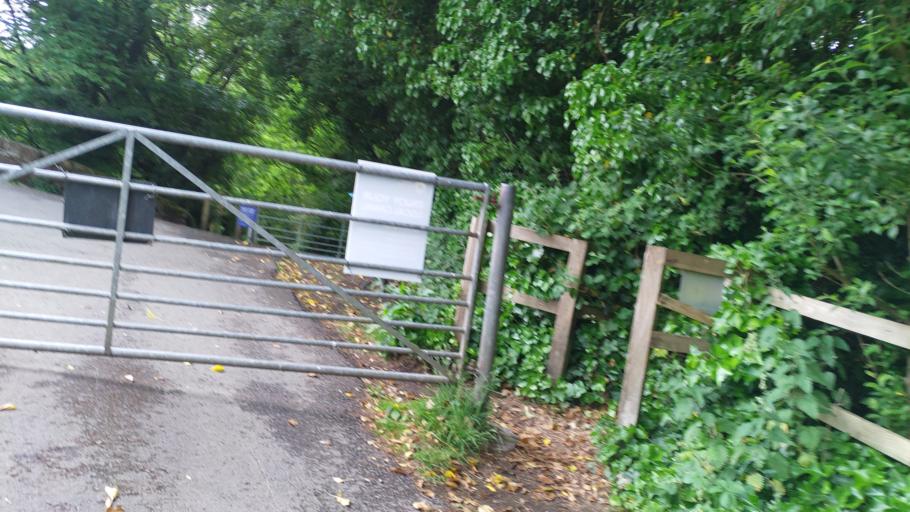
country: GB
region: England
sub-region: Lancashire
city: Chorley
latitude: 53.7038
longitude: -2.5911
